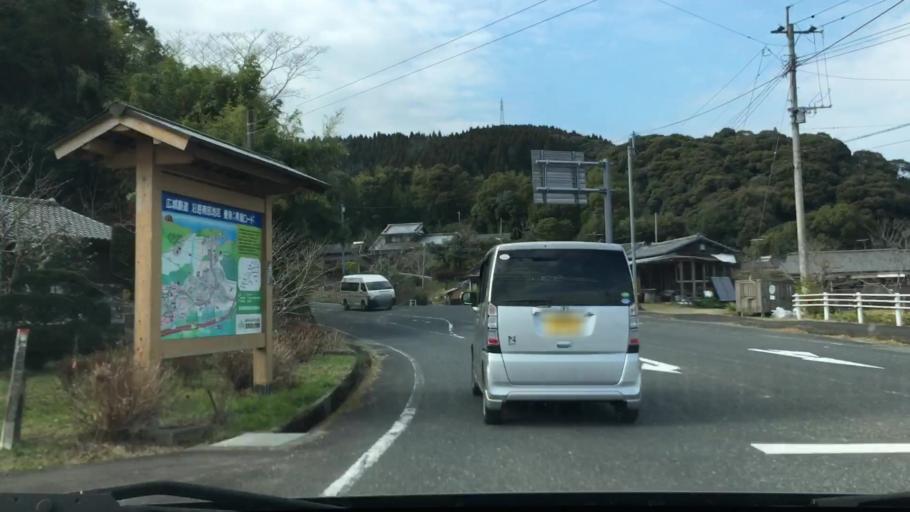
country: JP
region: Miyazaki
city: Nichinan
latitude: 31.6295
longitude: 131.3413
